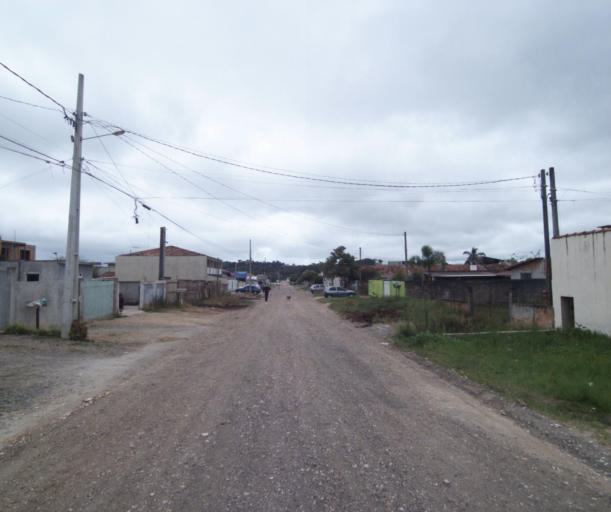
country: BR
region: Parana
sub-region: Quatro Barras
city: Quatro Barras
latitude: -25.3600
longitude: -49.0985
